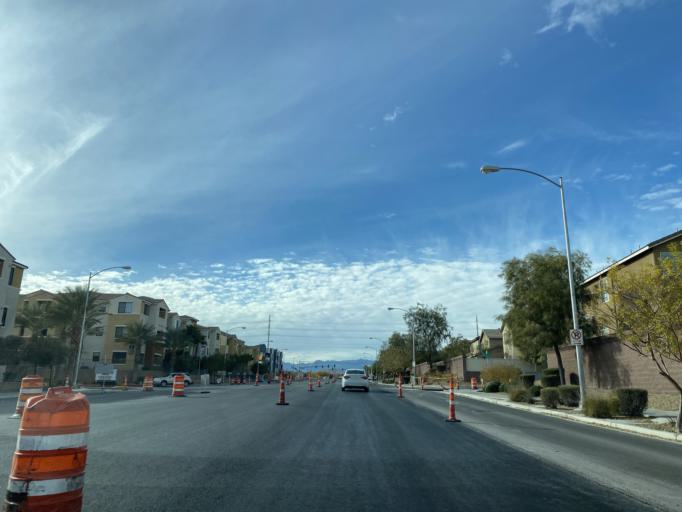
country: US
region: Nevada
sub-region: Clark County
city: Enterprise
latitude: 36.0415
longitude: -115.2397
